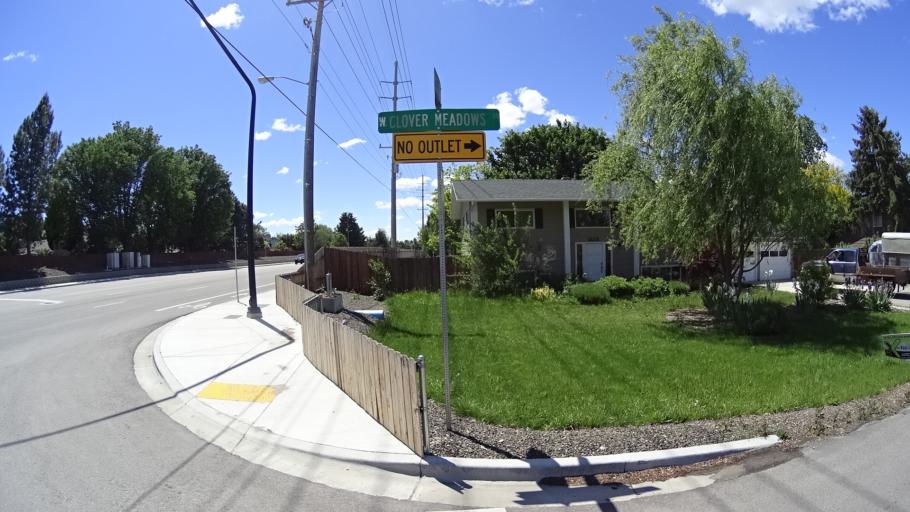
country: US
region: Idaho
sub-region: Ada County
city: Meridian
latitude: 43.6249
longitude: -116.3347
